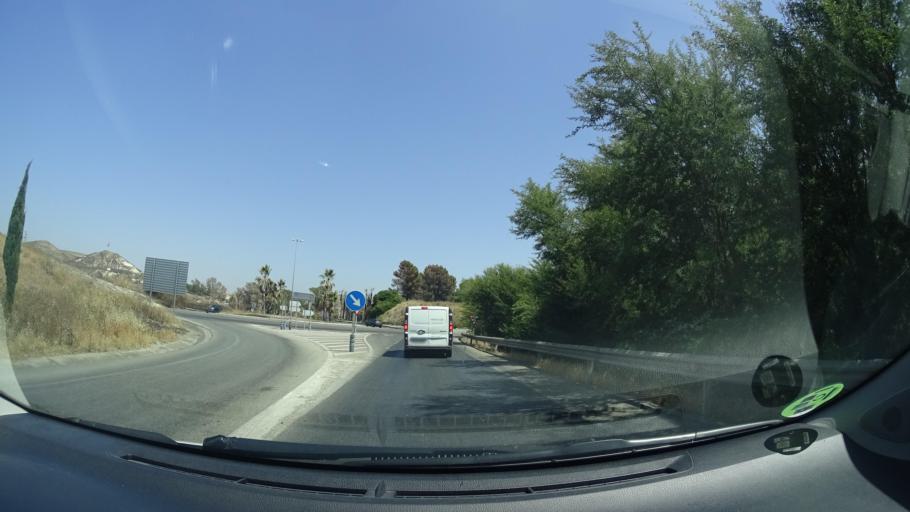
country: ES
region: Andalusia
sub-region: Provincia de Cadiz
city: Jerez de la Frontera
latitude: 36.6538
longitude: -6.0904
